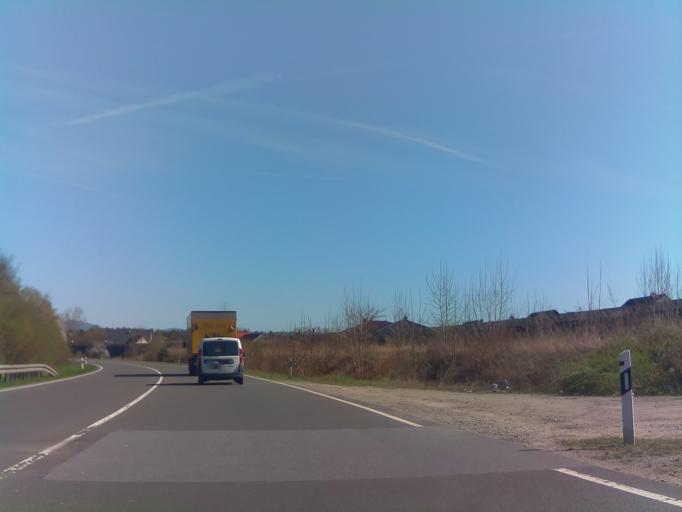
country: DE
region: Hesse
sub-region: Regierungsbezirk Darmstadt
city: Burstadt
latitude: 49.6376
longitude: 8.4715
